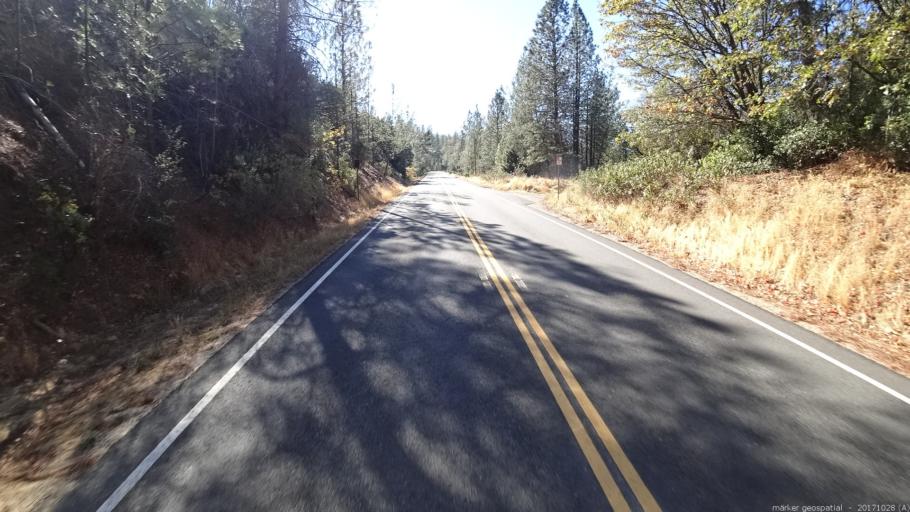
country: US
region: California
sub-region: Shasta County
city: Shasta
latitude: 40.6074
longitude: -122.5284
